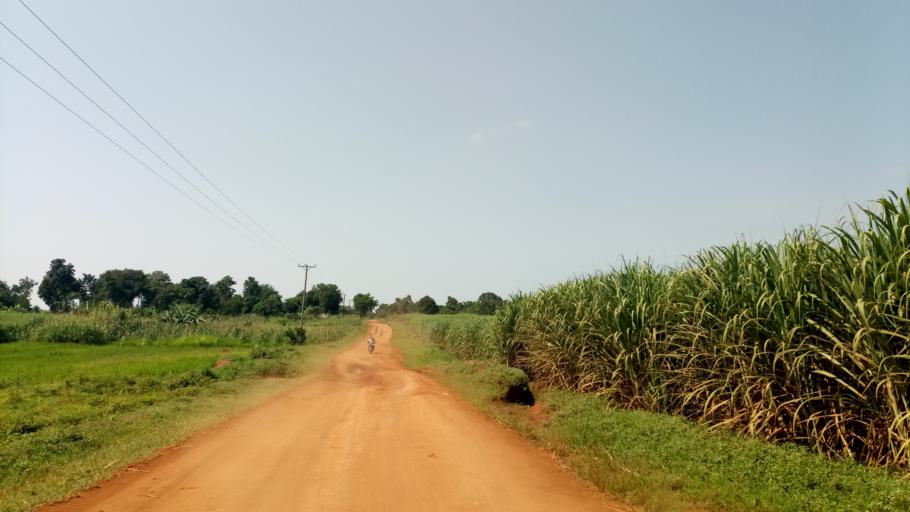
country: UG
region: Eastern Region
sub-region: Kaliro District
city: Kaliro
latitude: 0.9735
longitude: 33.4614
